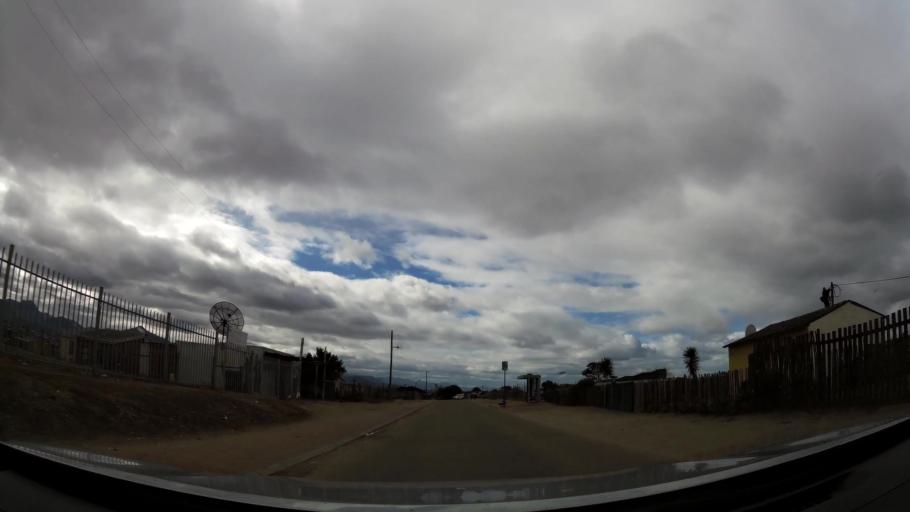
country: ZA
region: Western Cape
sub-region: Eden District Municipality
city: George
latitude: -34.0162
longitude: 22.4747
